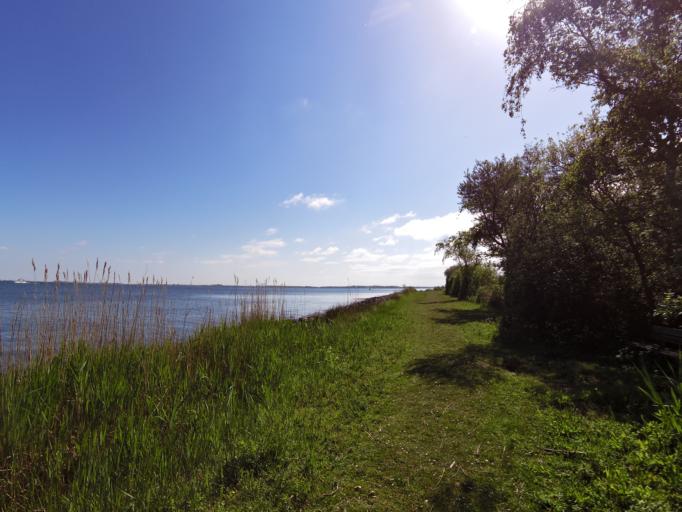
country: NL
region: South Holland
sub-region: Gemeente Goeree-Overflakkee
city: Ouddorp
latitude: 51.7835
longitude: 3.8939
